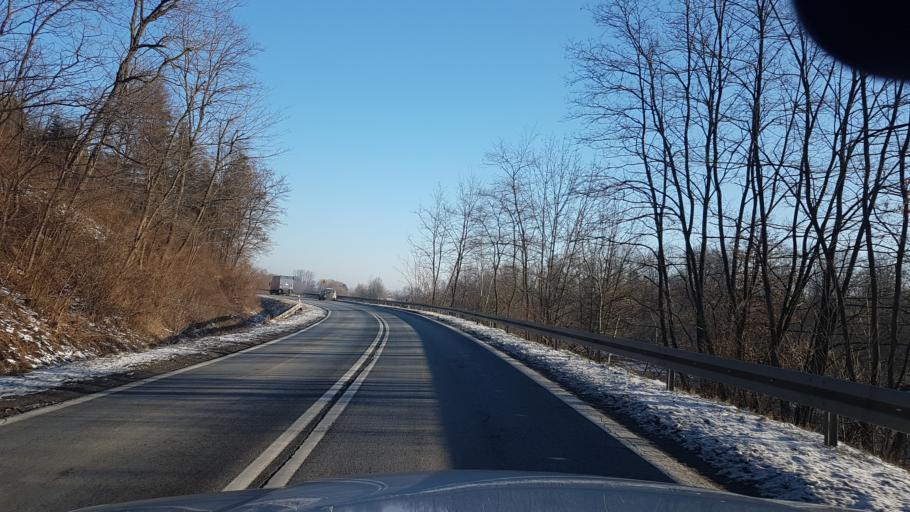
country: PL
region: Lesser Poland Voivodeship
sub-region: Powiat nowosadecki
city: Podegrodzie
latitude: 49.5424
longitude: 20.5599
